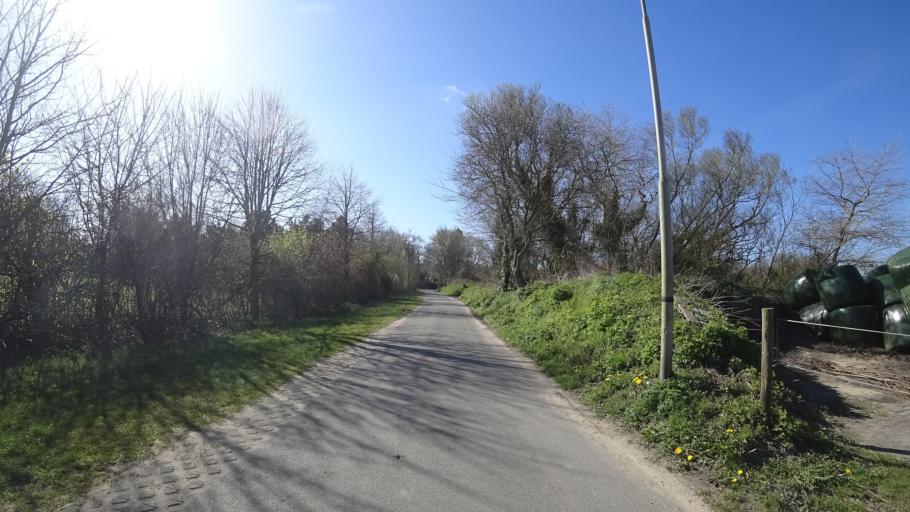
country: NL
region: South Holland
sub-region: Gemeente Goeree-Overflakkee
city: Ouddorp
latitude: 51.8153
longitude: 3.9129
